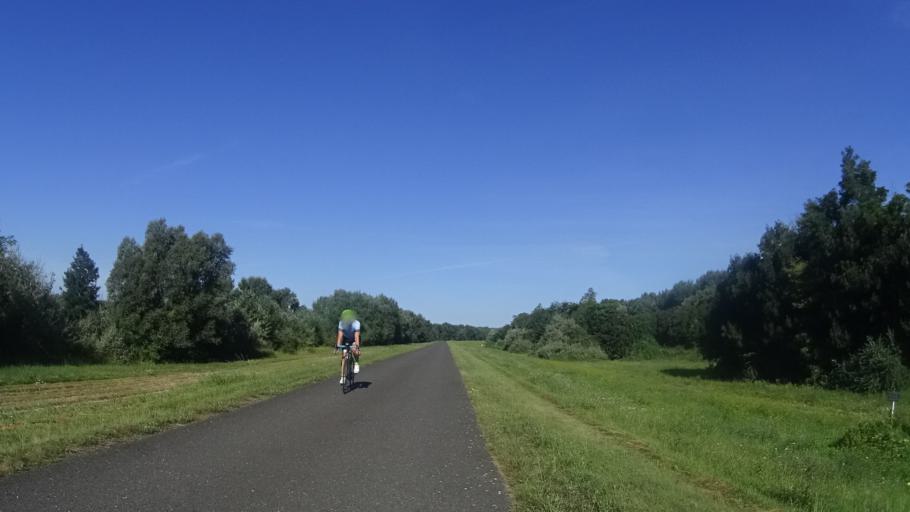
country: HU
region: Gyor-Moson-Sopron
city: Rajka
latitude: 48.0627
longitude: 17.1855
